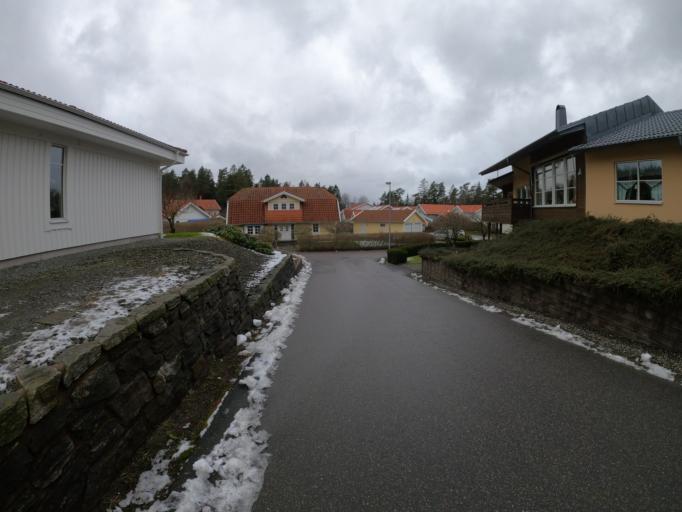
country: SE
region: Vaestra Goetaland
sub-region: Harryda Kommun
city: Molnlycke
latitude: 57.6419
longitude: 12.1134
